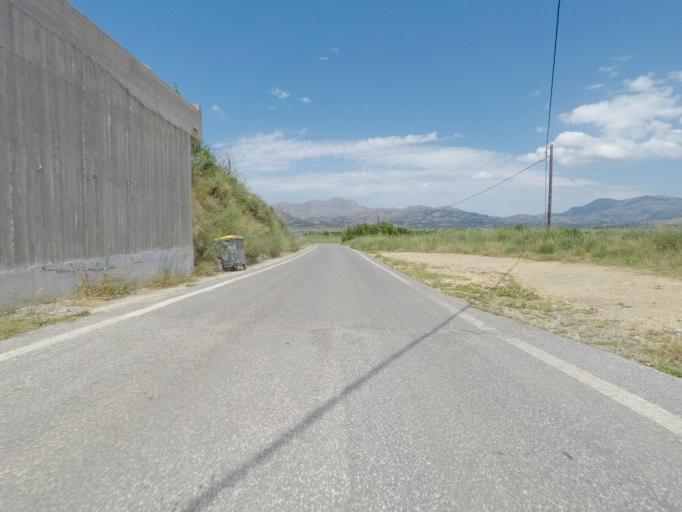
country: GR
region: Crete
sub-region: Nomos Irakleiou
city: Mokhos
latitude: 35.1765
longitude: 25.4401
